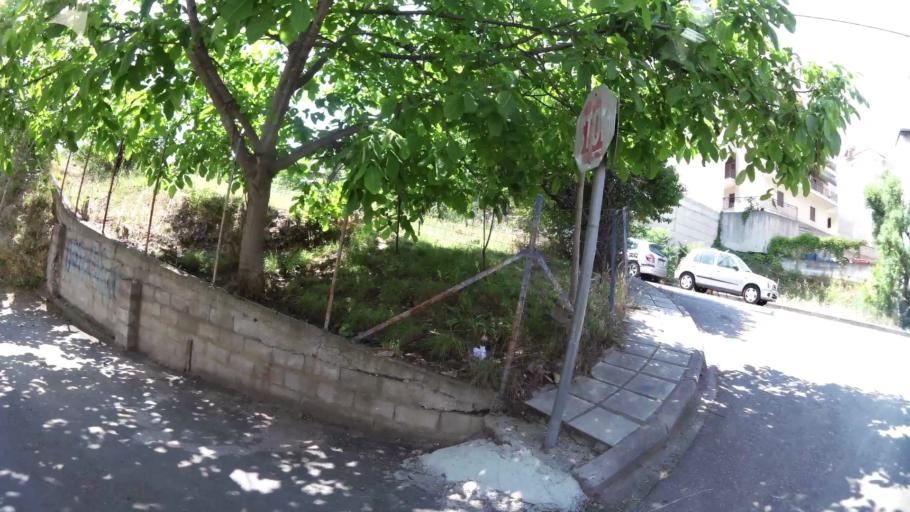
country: GR
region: Central Macedonia
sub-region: Nomos Imathias
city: Veroia
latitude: 40.5125
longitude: 22.2098
